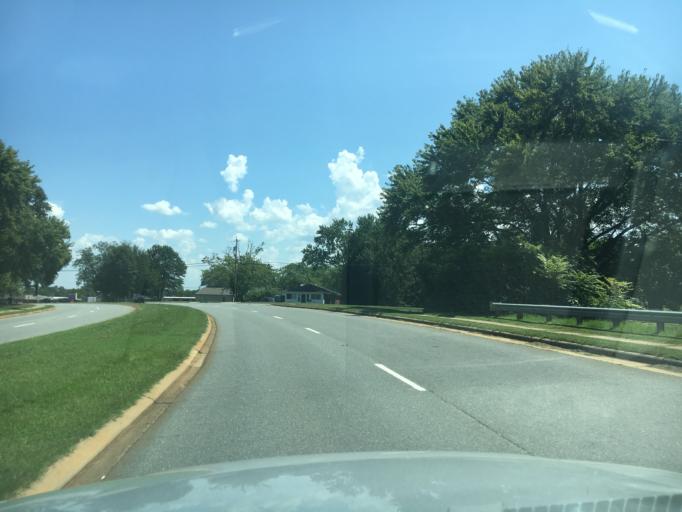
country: US
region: North Carolina
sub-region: Rutherford County
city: Forest City
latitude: 35.3283
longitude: -81.8645
